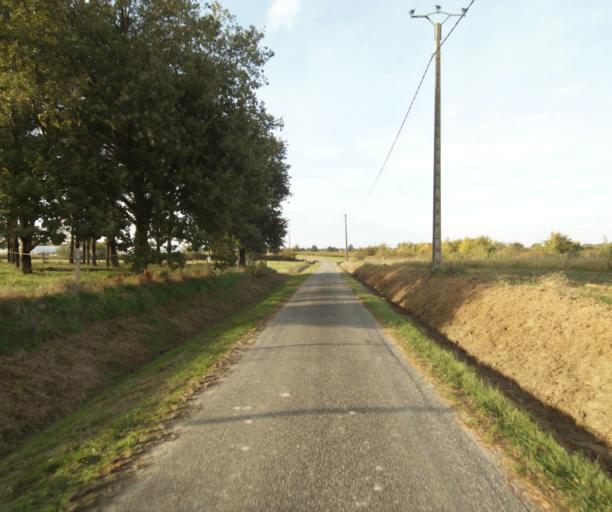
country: FR
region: Midi-Pyrenees
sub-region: Departement du Tarn-et-Garonne
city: Campsas
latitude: 43.8791
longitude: 1.3487
